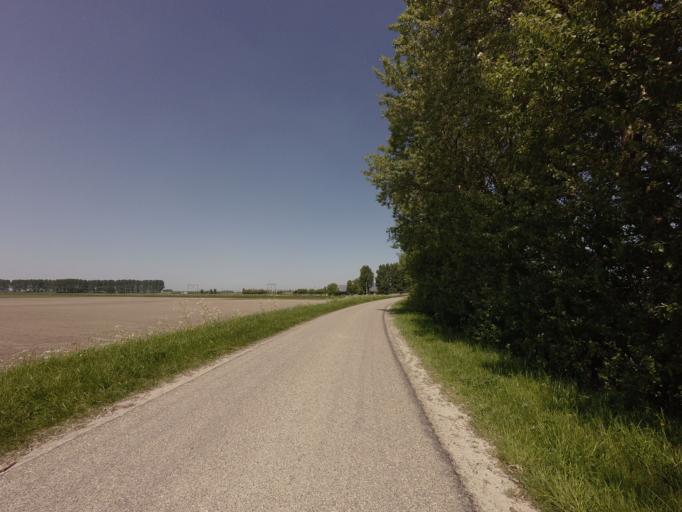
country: NL
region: Zeeland
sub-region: Gemeente Borsele
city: Borssele
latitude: 51.4991
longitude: 3.7874
